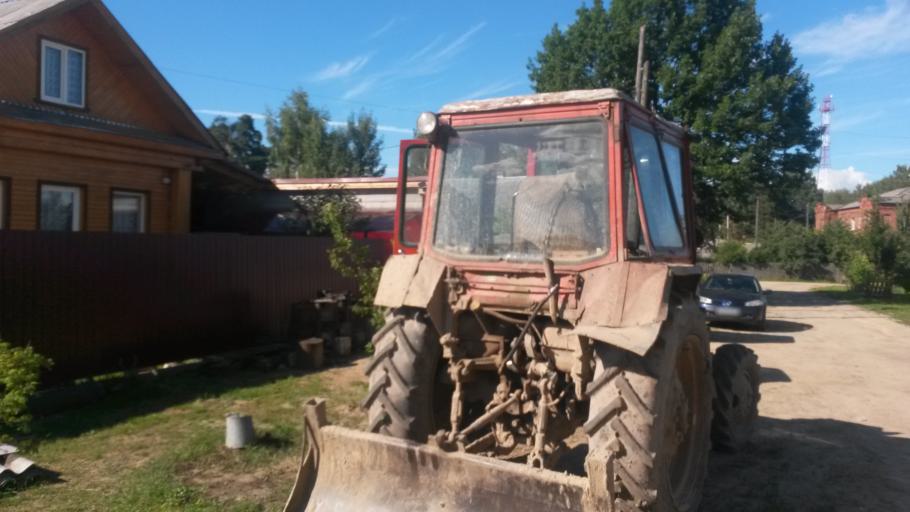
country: RU
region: Ivanovo
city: Zarechnyy
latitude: 57.4967
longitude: 42.3295
